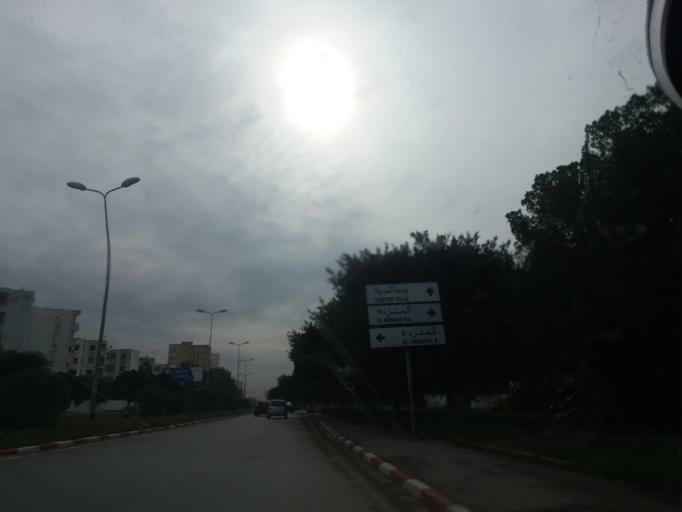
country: TN
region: Tunis
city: Tunis
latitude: 36.8484
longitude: 10.1578
